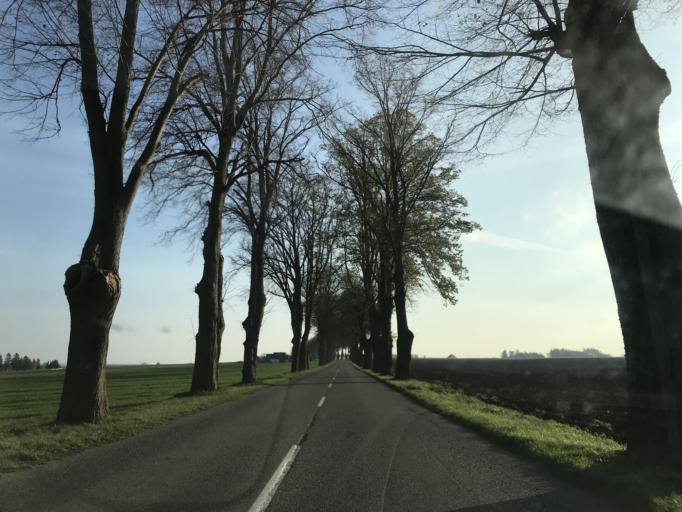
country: PL
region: Pomeranian Voivodeship
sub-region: Powiat pucki
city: Krokowa
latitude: 54.7857
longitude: 18.1230
